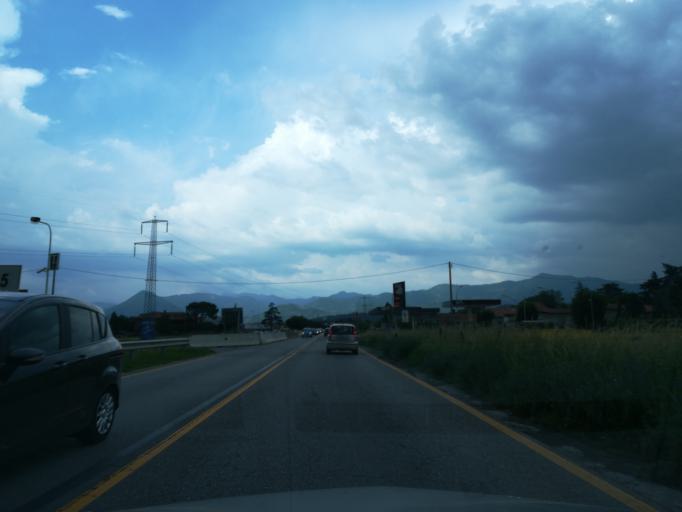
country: IT
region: Lombardy
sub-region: Provincia di Bergamo
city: Mozzo
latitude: 45.7037
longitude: 9.6053
